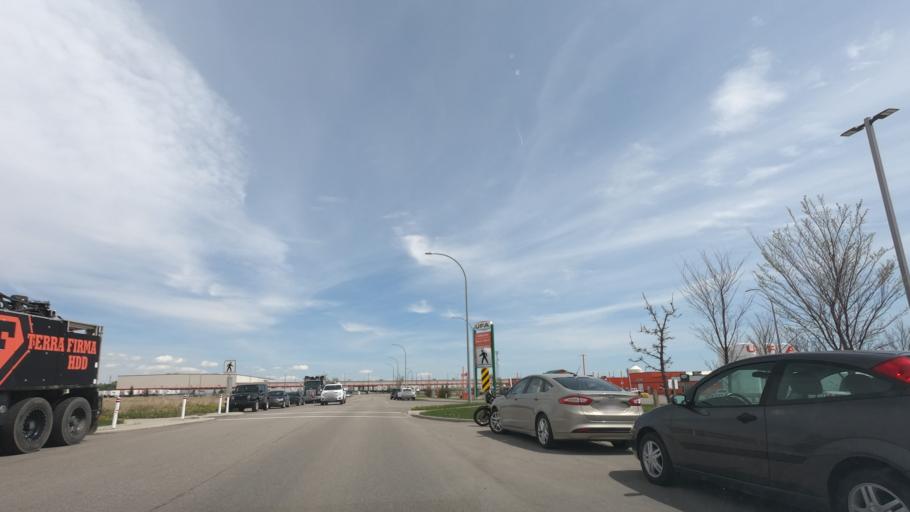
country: CA
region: Alberta
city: Airdrie
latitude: 51.3043
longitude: -113.9986
